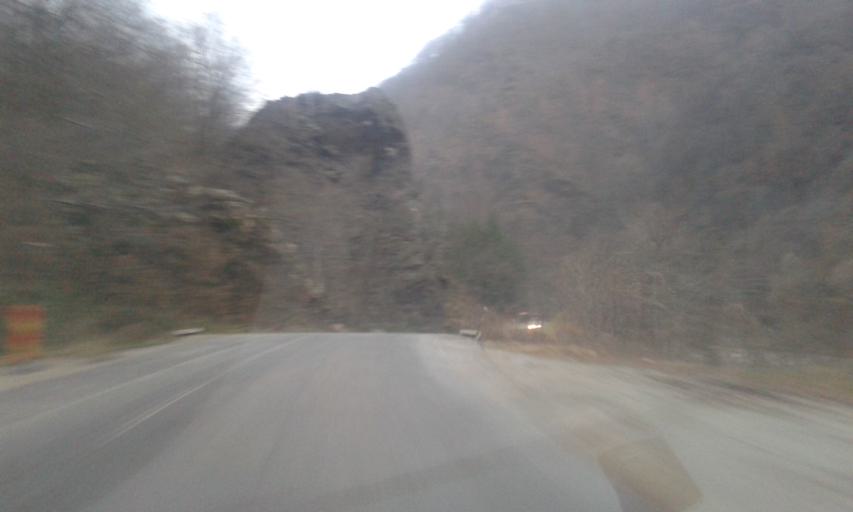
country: RO
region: Gorj
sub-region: Comuna Bumbesti-Jiu
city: Bumbesti-Jiu
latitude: 45.2555
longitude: 23.3892
